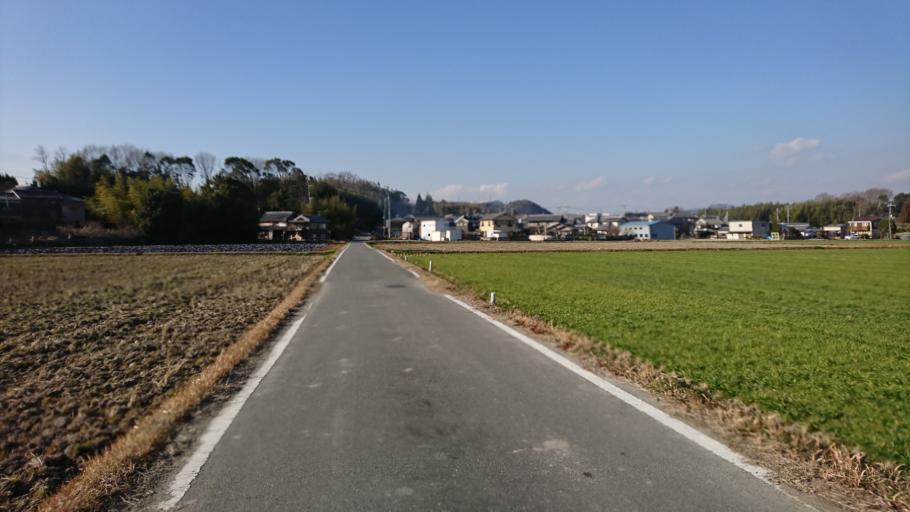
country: JP
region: Hyogo
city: Kakogawacho-honmachi
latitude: 34.7804
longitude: 134.8693
